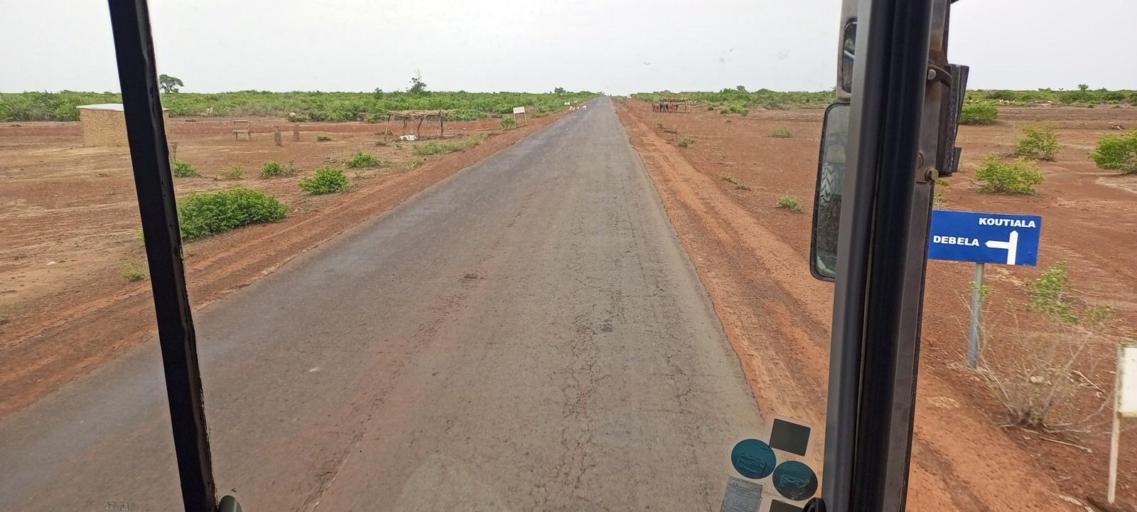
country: ML
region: Segou
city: Bla
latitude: 12.7057
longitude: -5.7242
